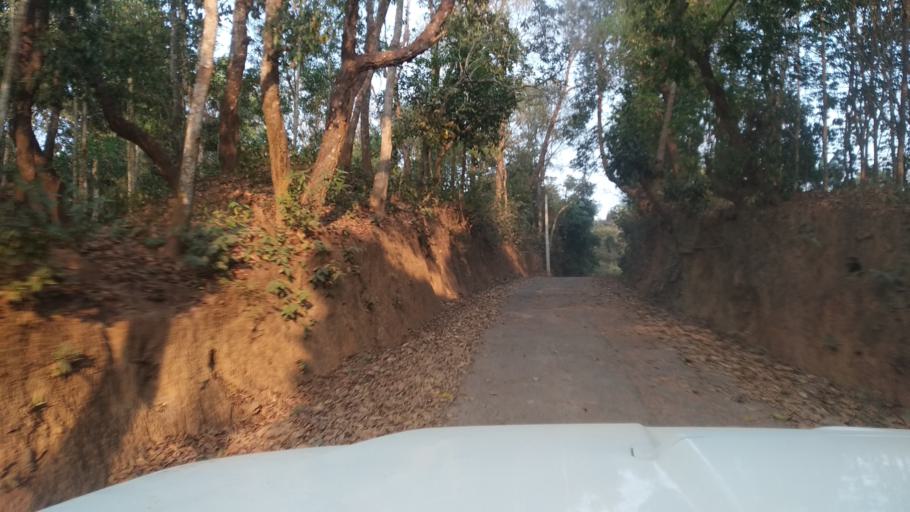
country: IN
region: Tripura
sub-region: South Tripura
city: Belonia
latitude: 23.3177
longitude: 91.3236
